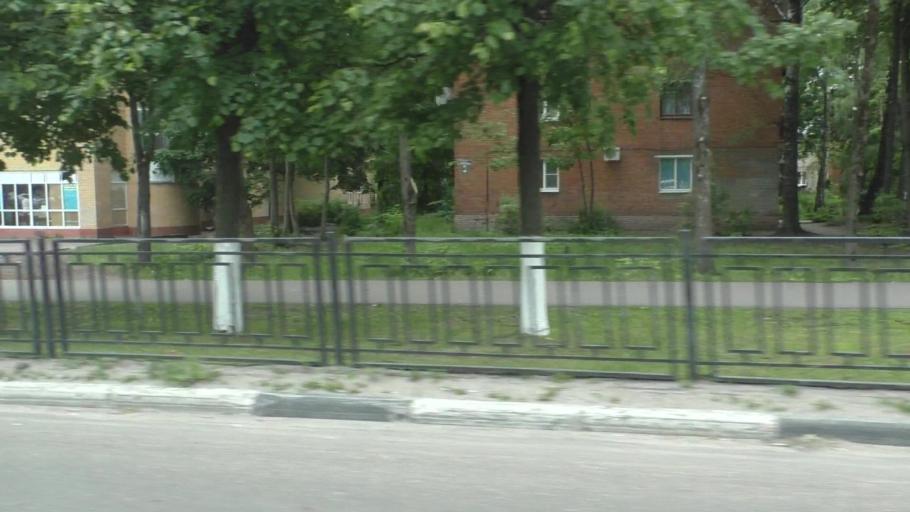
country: RU
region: Moskovskaya
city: Yegor'yevsk
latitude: 55.3729
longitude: 39.0536
